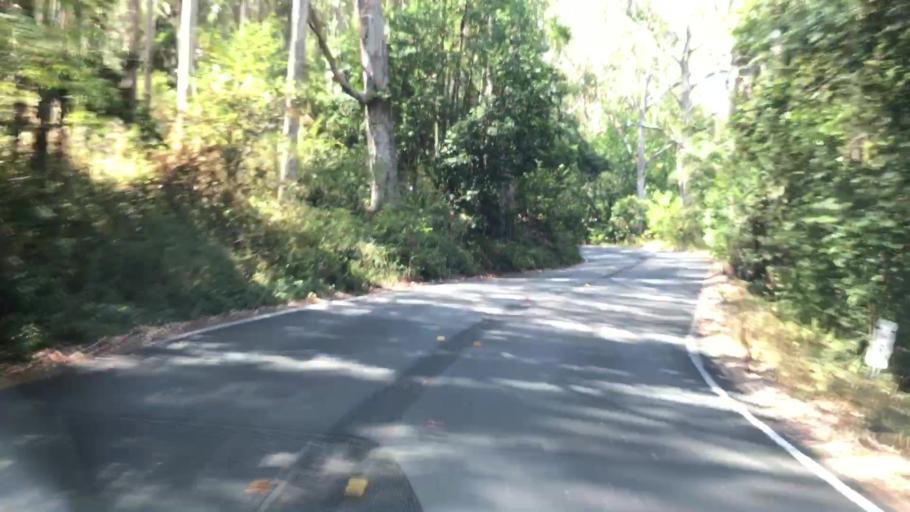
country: US
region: California
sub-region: Marin County
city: Bolinas
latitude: 37.9566
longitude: -122.7145
